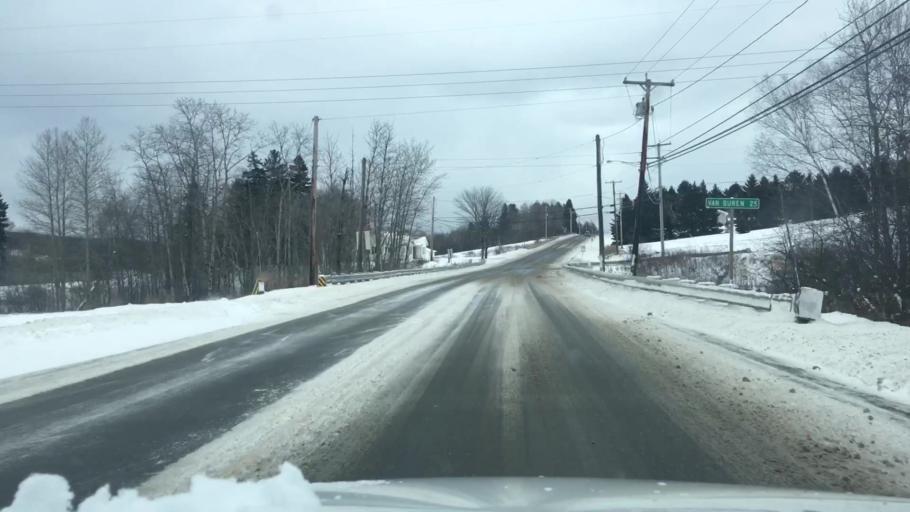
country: US
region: Maine
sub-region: Aroostook County
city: Madawaska
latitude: 47.3527
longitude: -68.2984
